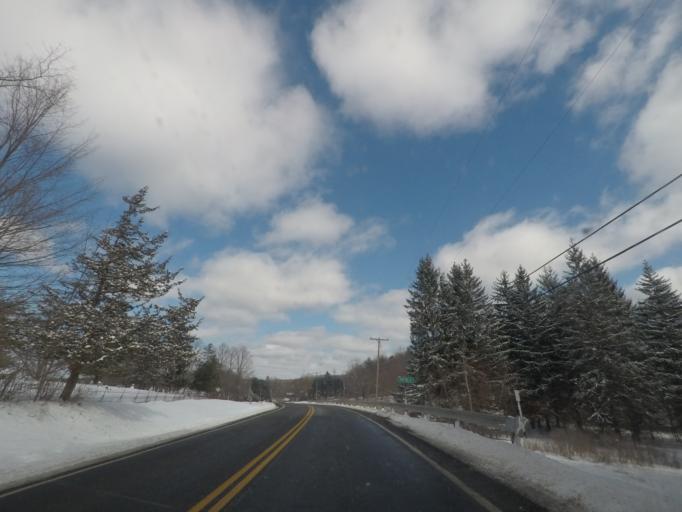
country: US
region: New York
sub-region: Rensselaer County
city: Nassau
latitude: 42.4612
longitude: -73.5418
